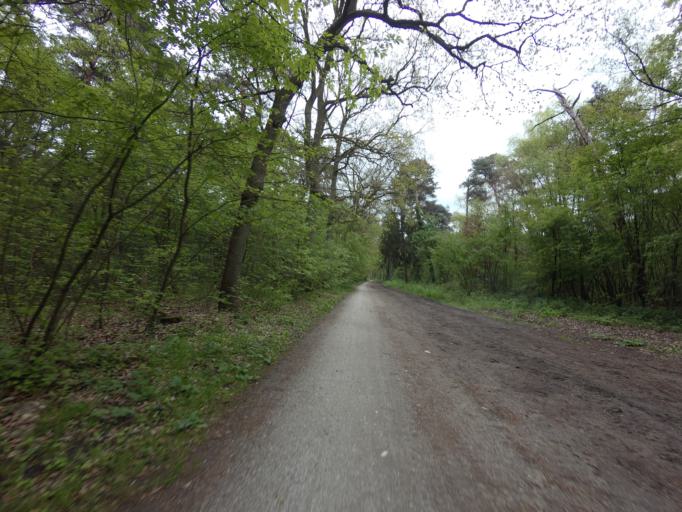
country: NL
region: Utrecht
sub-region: Gemeente De Bilt
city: De Bilt
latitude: 52.1358
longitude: 5.1887
